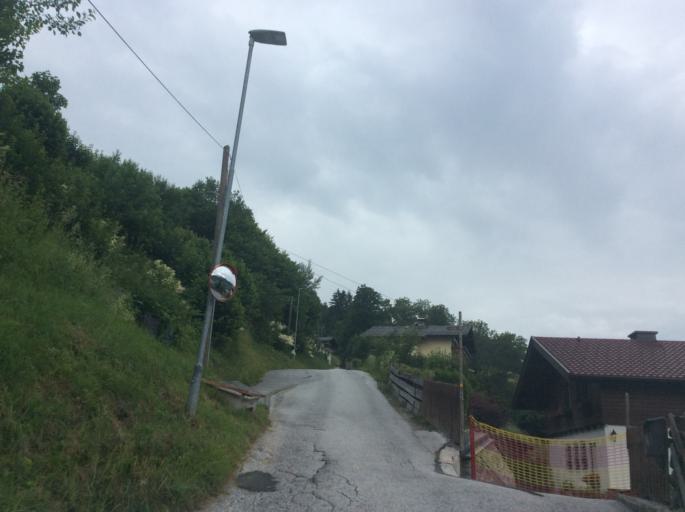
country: AT
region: Styria
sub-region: Politischer Bezirk Liezen
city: Schladming
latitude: 47.3893
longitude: 13.6810
